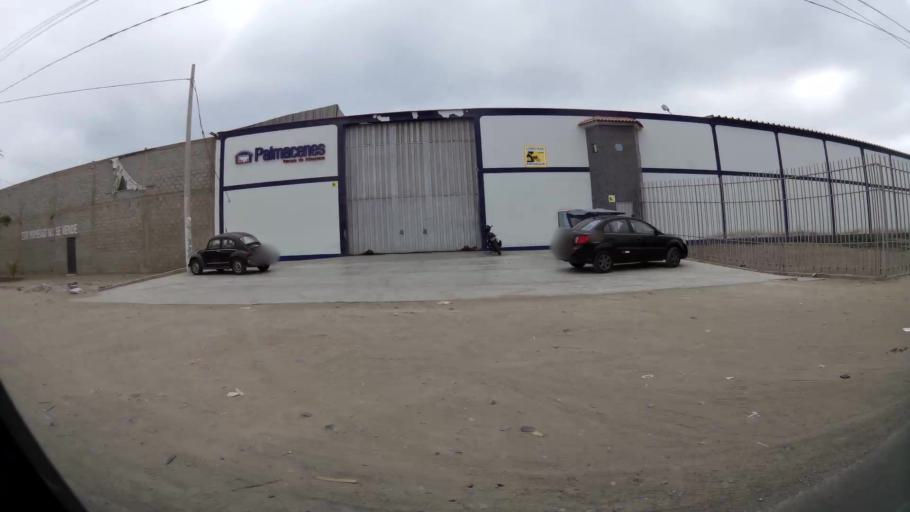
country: PE
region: La Libertad
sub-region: Provincia de Trujillo
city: Huanchaco
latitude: -8.0877
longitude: -79.0948
